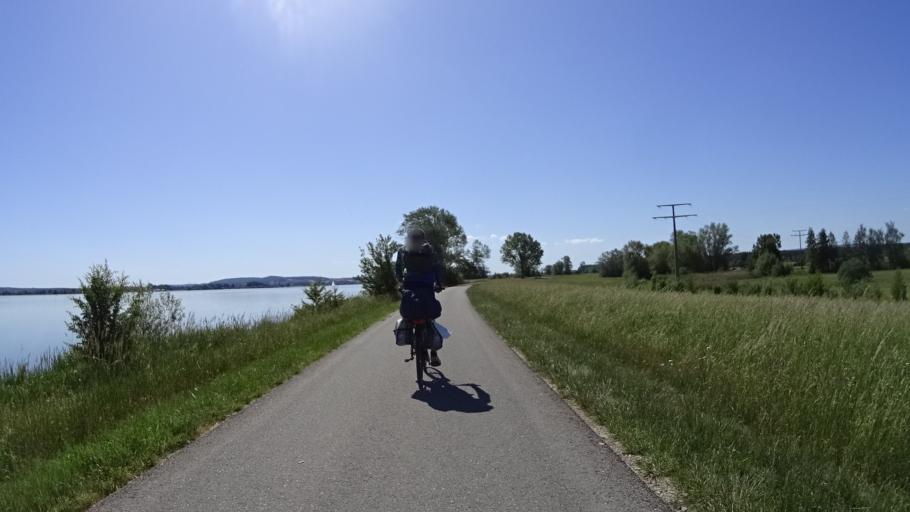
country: DE
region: Bavaria
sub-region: Regierungsbezirk Mittelfranken
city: Muhr am See
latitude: 49.1337
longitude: 10.7126
